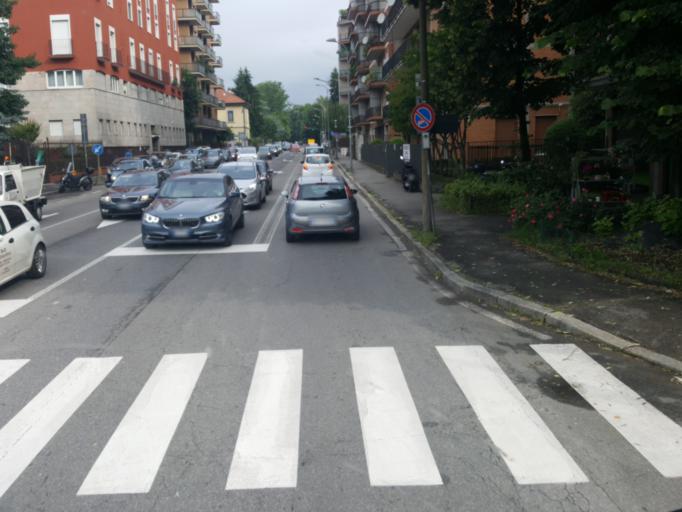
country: IT
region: Lombardy
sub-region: Provincia di Monza e Brianza
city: Monza
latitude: 45.5882
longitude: 9.2853
